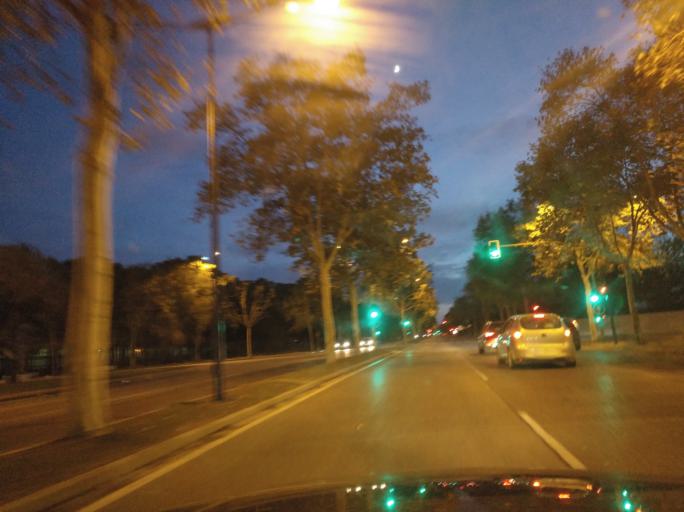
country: ES
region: Andalusia
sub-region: Provincia de Sevilla
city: Camas
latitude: 37.4064
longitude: -6.0098
